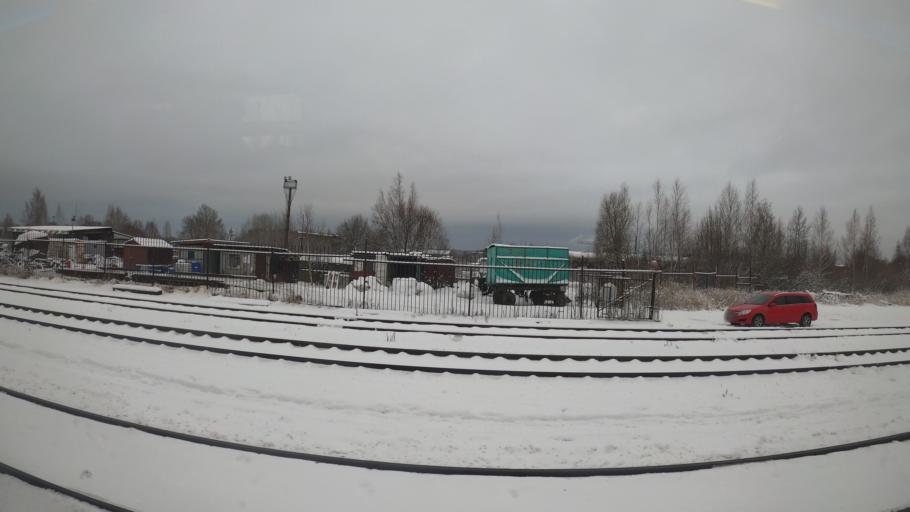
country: RU
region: Jaroslavl
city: Pereslavl'-Zalesskiy
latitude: 56.7350
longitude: 38.8880
